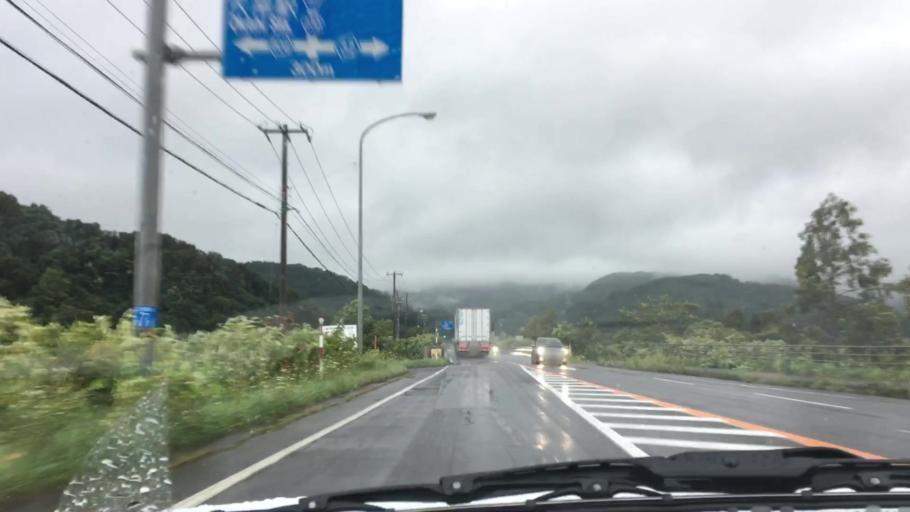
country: JP
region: Hokkaido
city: Niseko Town
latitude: 42.5987
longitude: 140.6388
